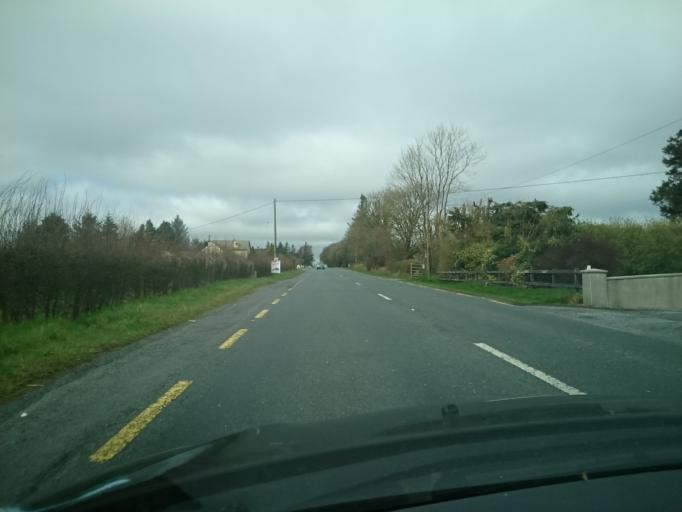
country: IE
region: Connaught
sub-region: Maigh Eo
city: Claremorris
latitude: 53.7410
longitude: -9.0135
